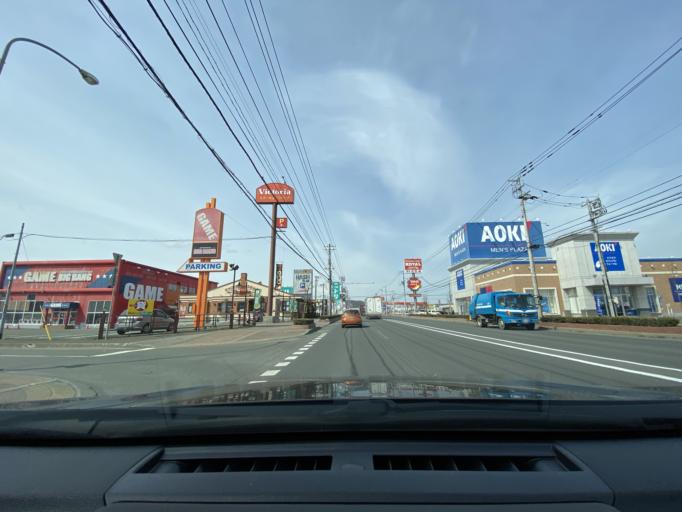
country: JP
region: Hokkaido
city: Kitami
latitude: 43.7976
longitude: 143.8521
